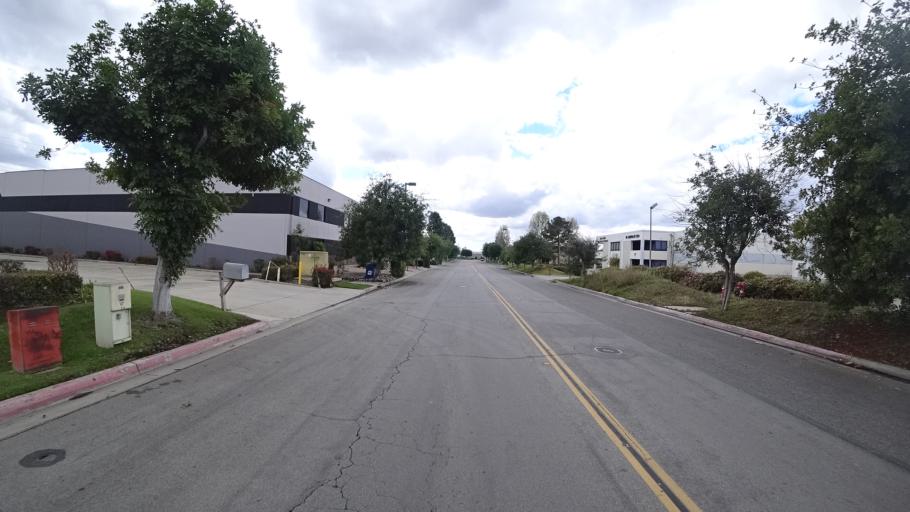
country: US
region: California
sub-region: Los Angeles County
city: Baldwin Park
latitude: 34.0976
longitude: -117.9825
